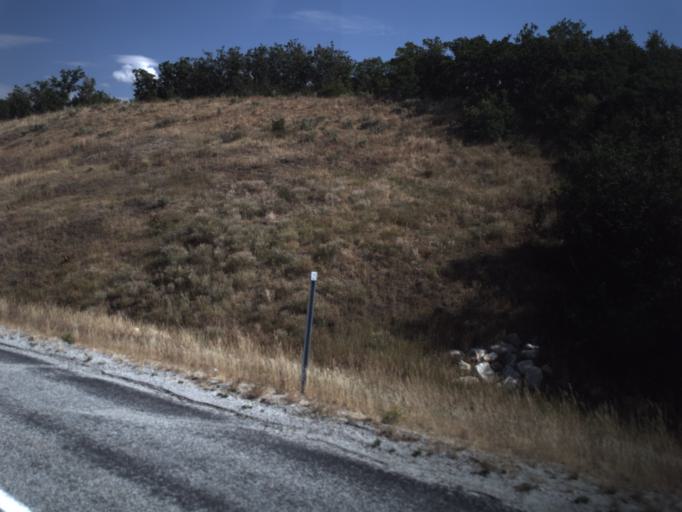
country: US
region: Utah
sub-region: Morgan County
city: Mountain Green
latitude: 41.2051
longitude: -111.8271
